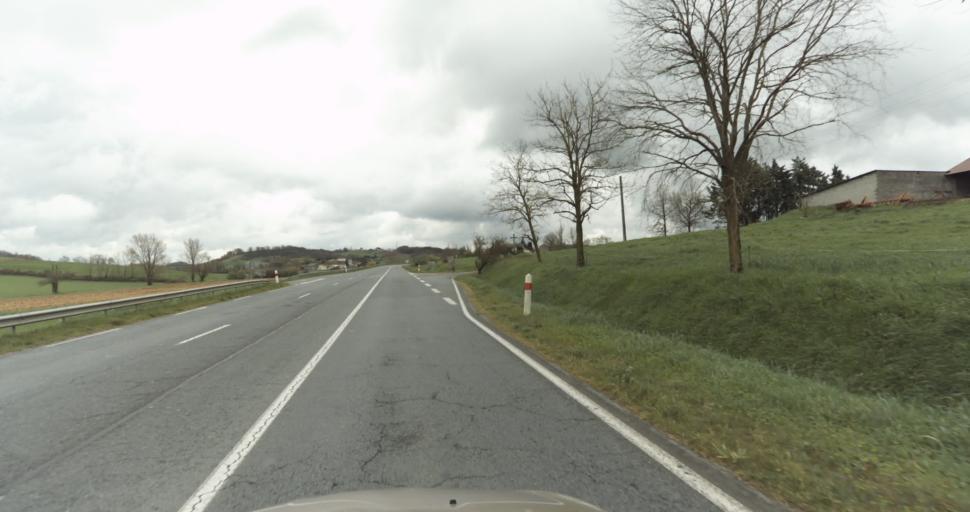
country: FR
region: Midi-Pyrenees
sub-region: Departement du Tarn
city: Puygouzon
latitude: 43.8798
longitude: 2.1735
